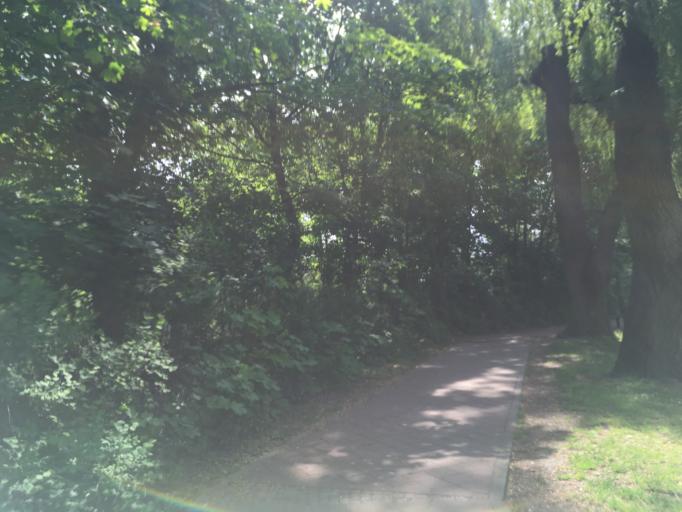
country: DE
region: Brandenburg
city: Werneuchen
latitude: 52.6342
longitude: 13.7388
